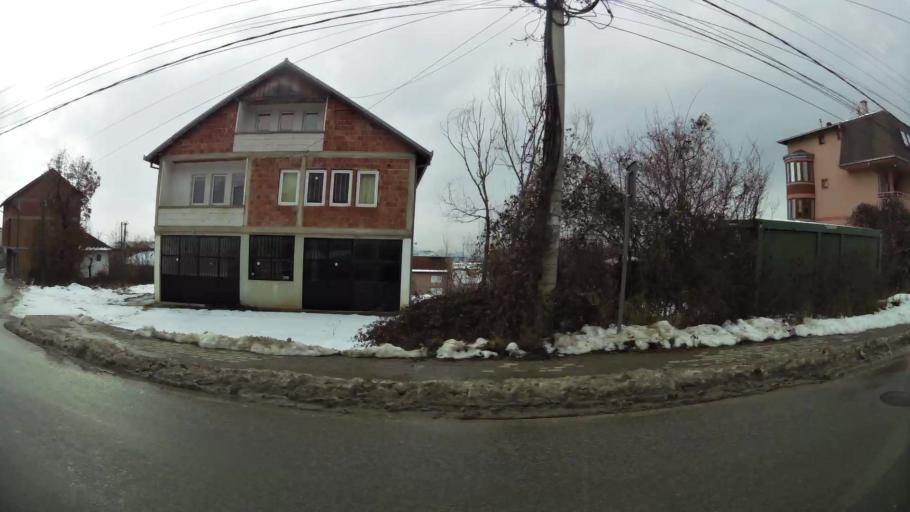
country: XK
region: Pristina
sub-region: Komuna e Prishtines
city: Pristina
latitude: 42.6505
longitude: 21.1938
